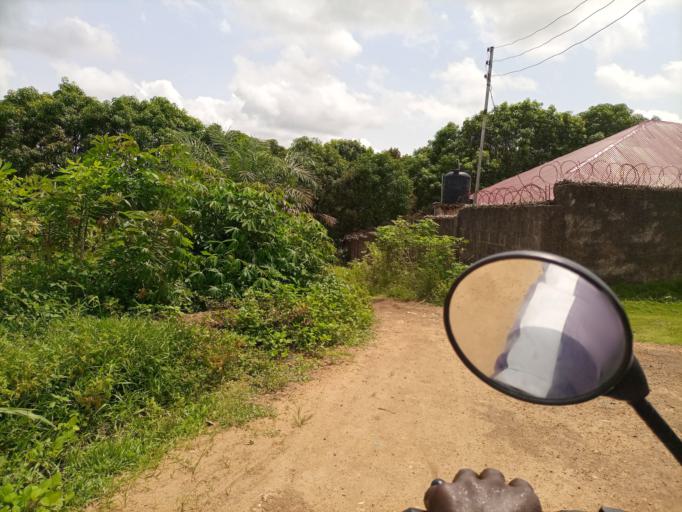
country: SL
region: Southern Province
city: Bo
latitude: 7.9759
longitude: -11.7649
